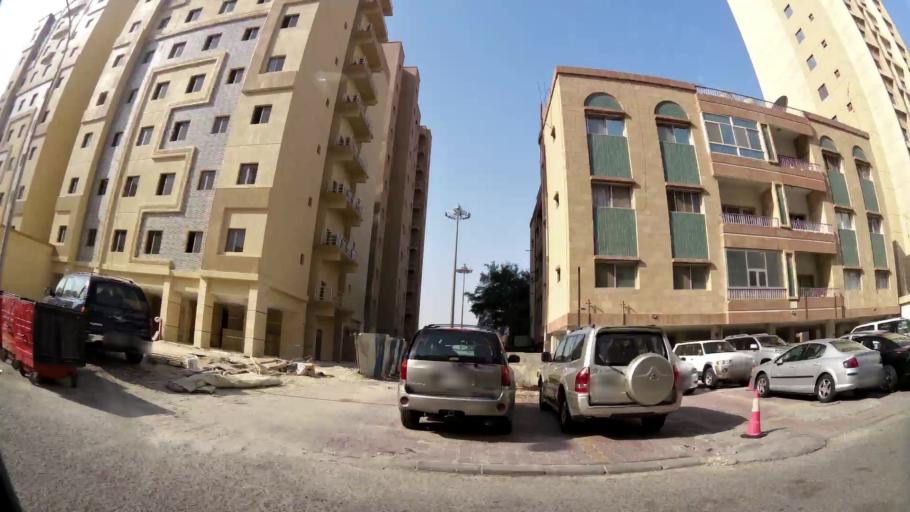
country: KW
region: Muhafazat Hawalli
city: Hawalli
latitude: 29.3374
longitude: 48.0062
